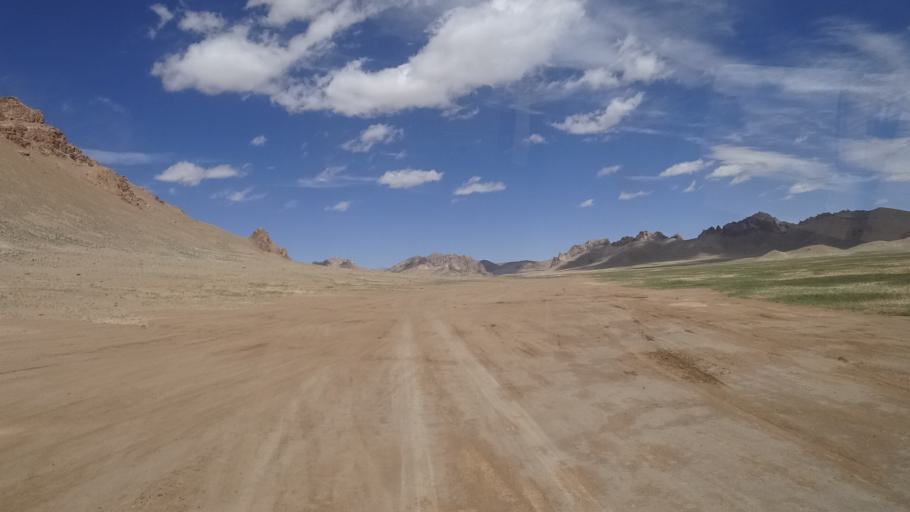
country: TJ
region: Gorno-Badakhshan
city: Murghob
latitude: 37.7724
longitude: 74.1999
